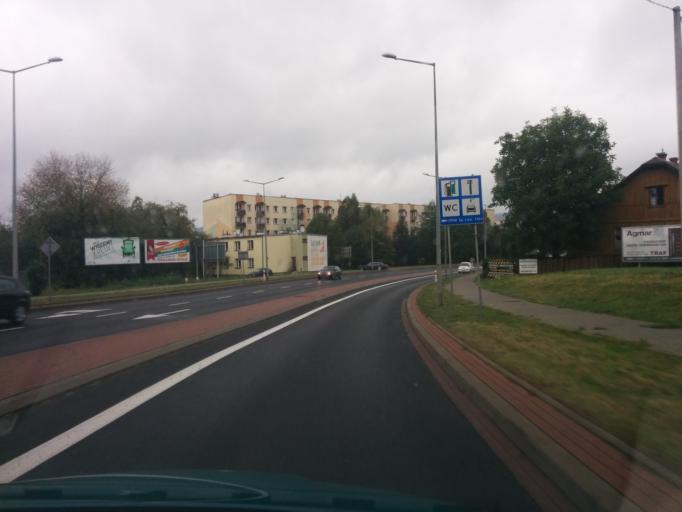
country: PL
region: Subcarpathian Voivodeship
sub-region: Powiat sanocki
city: Sanok
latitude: 49.5653
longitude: 22.1944
